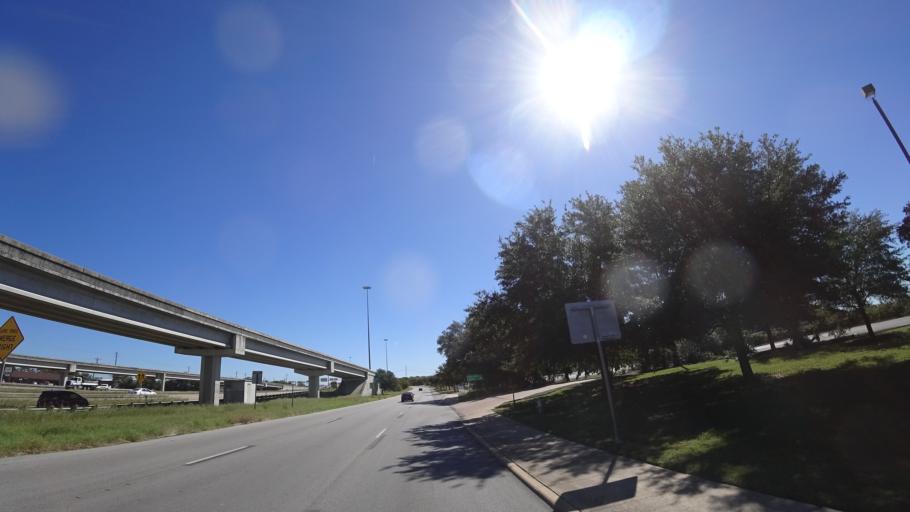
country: US
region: Texas
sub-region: Travis County
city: Rollingwood
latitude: 30.2326
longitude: -97.8099
